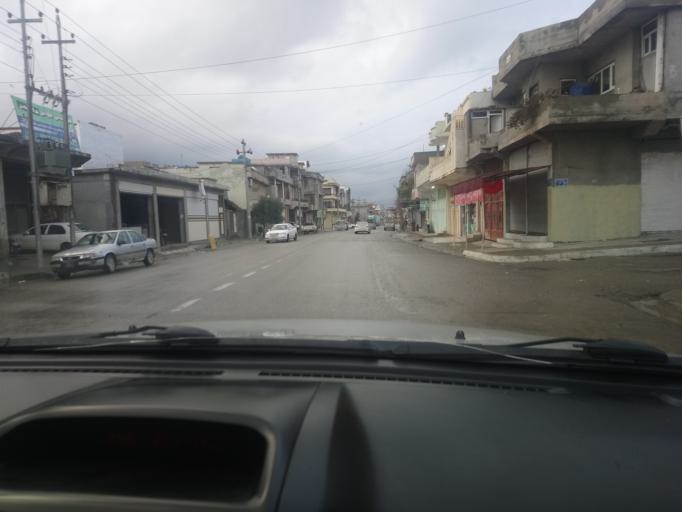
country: IQ
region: As Sulaymaniyah
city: Qeladize
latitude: 36.1837
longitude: 45.1322
